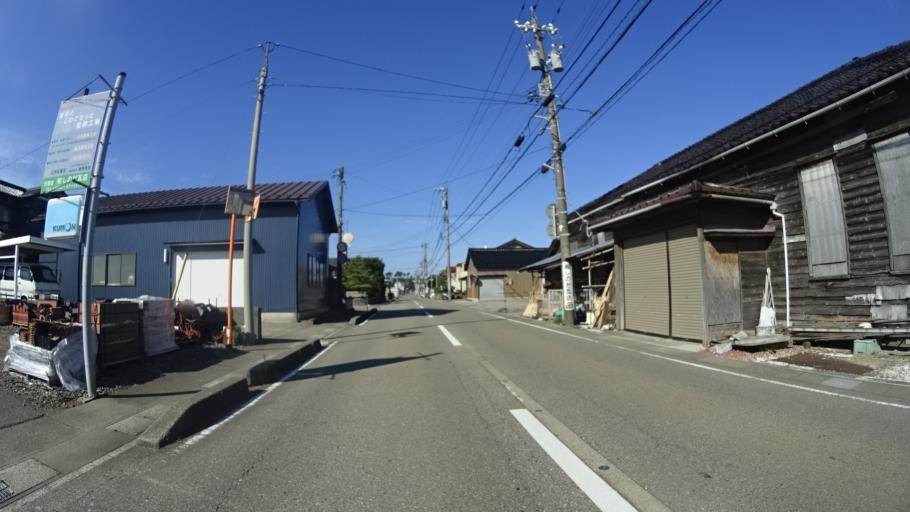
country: JP
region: Ishikawa
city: Kanazawa-shi
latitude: 36.6074
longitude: 136.6062
